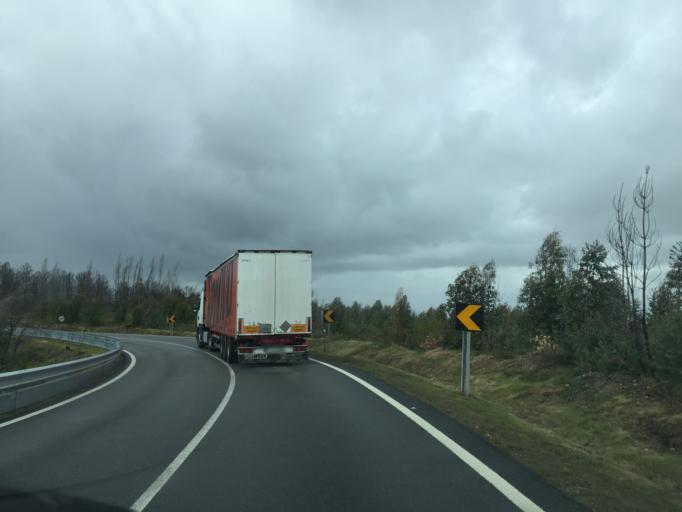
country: PT
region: Coimbra
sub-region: Oliveira do Hospital
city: Oliveira do Hospital
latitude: 40.3258
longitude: -7.9314
